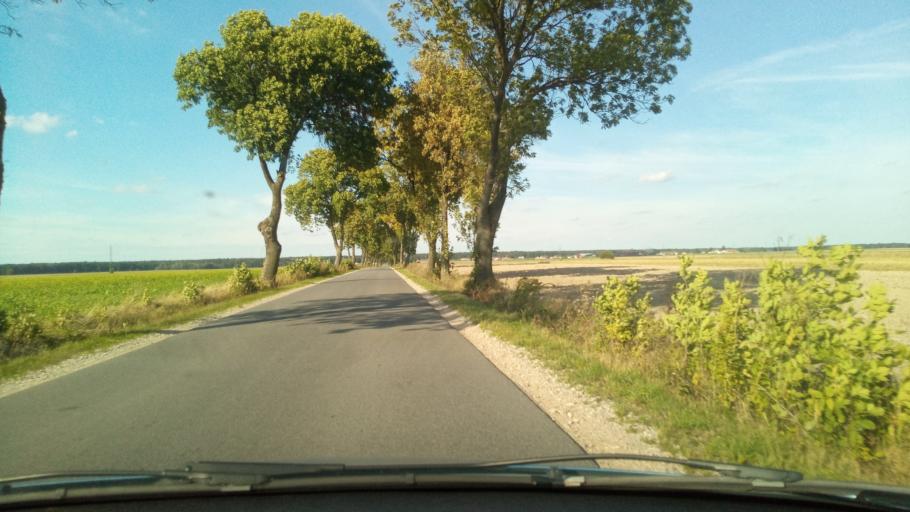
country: PL
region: Lodz Voivodeship
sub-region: Powiat piotrkowski
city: Sulejow
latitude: 51.3889
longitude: 19.8201
